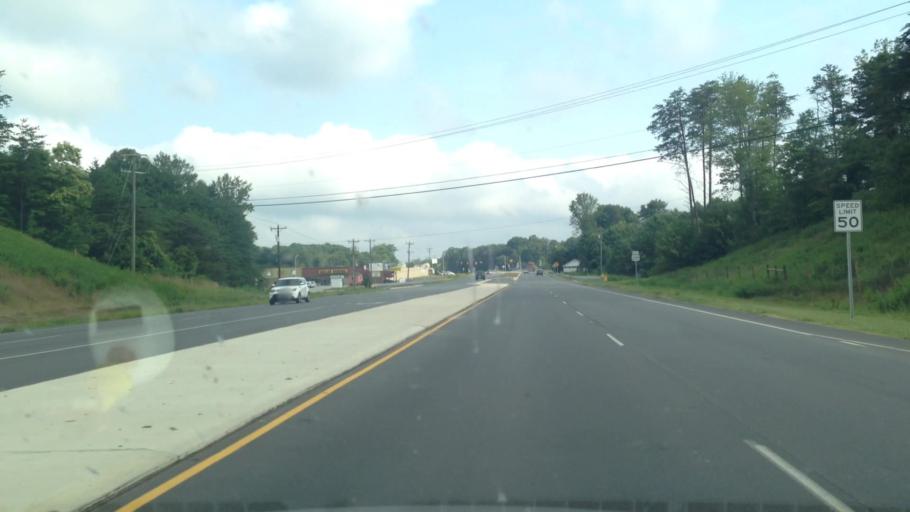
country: US
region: North Carolina
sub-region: Guilford County
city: Summerfield
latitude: 36.1890
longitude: -79.8901
